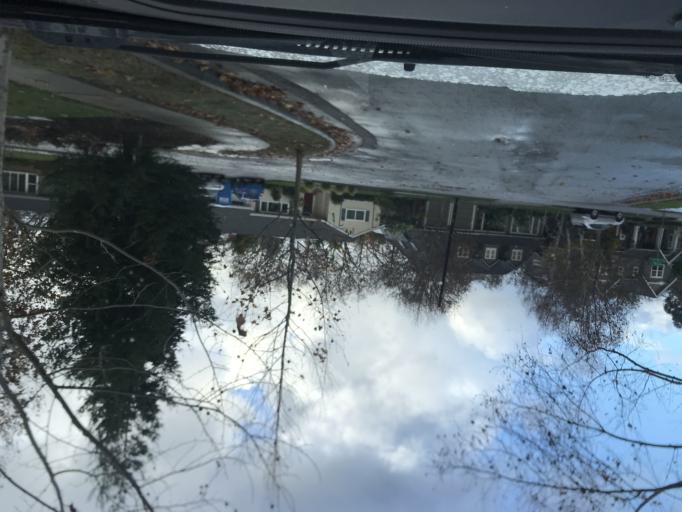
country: US
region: California
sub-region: Santa Clara County
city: Buena Vista
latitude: 37.3060
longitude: -121.9103
